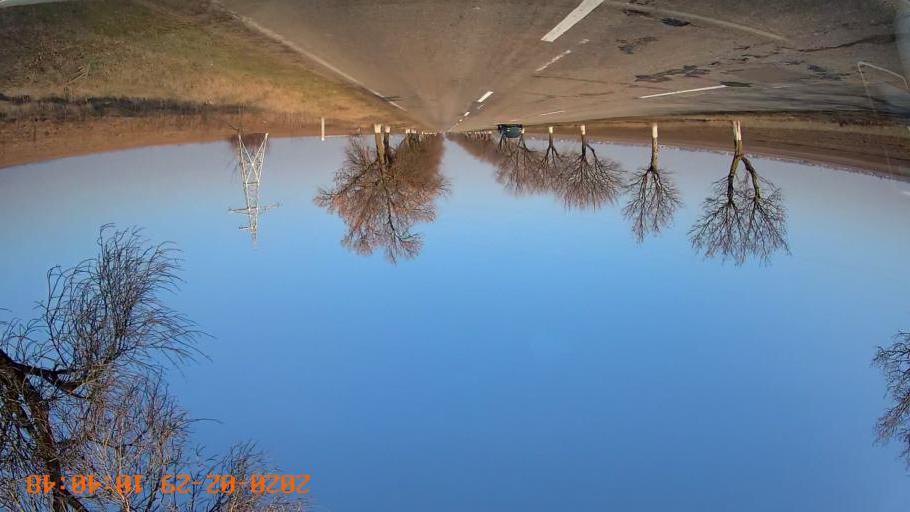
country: MD
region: Anenii Noi
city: Varnita
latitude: 47.0363
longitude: 29.4345
